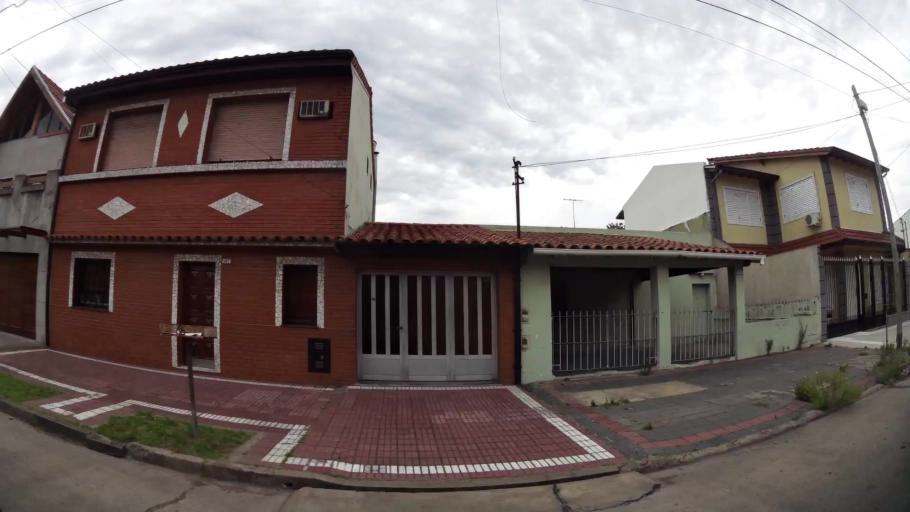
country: AR
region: Buenos Aires
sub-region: Partido de Lanus
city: Lanus
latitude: -34.6859
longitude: -58.3939
